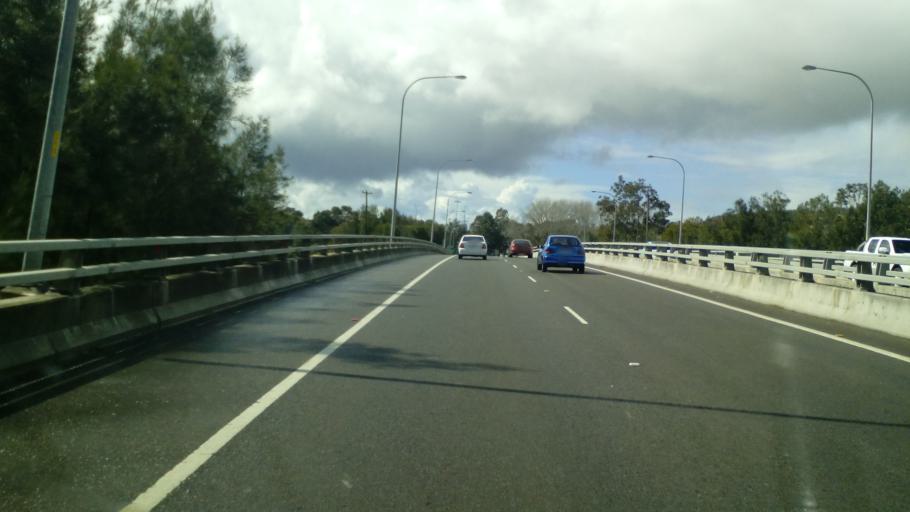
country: AU
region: New South Wales
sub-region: Lake Macquarie Shire
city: Fennell Bay
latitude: -32.9596
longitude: 151.6139
